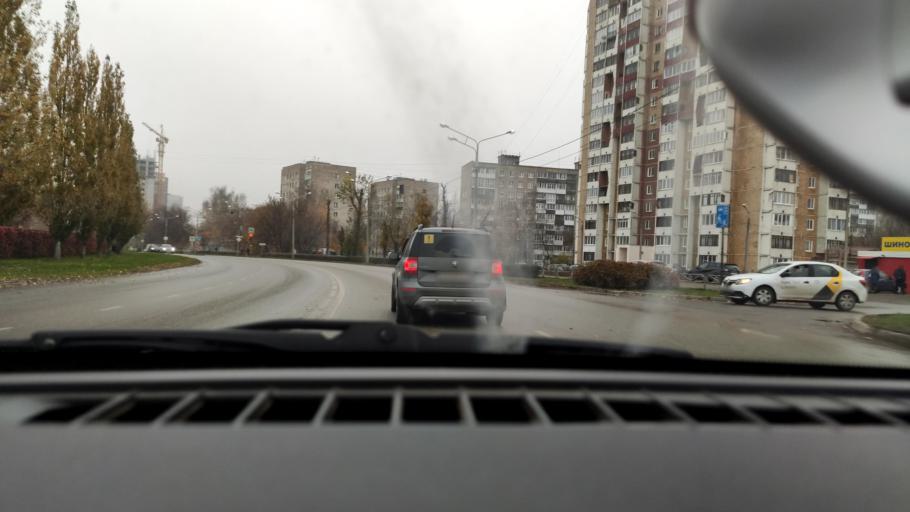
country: RU
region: Perm
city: Perm
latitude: 57.9769
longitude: 56.2146
